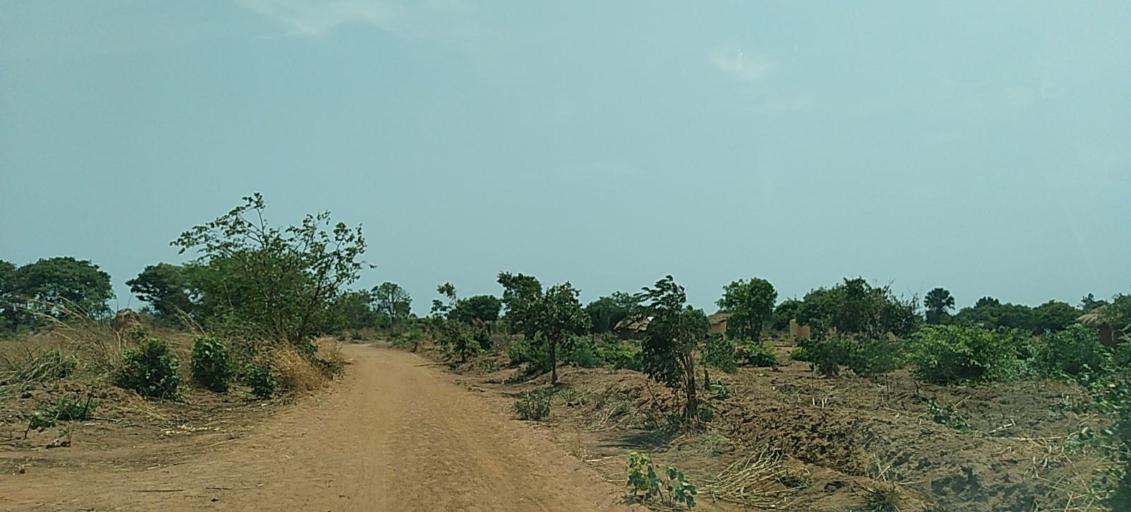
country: ZM
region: Copperbelt
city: Ndola
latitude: -13.0464
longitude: 28.7379
